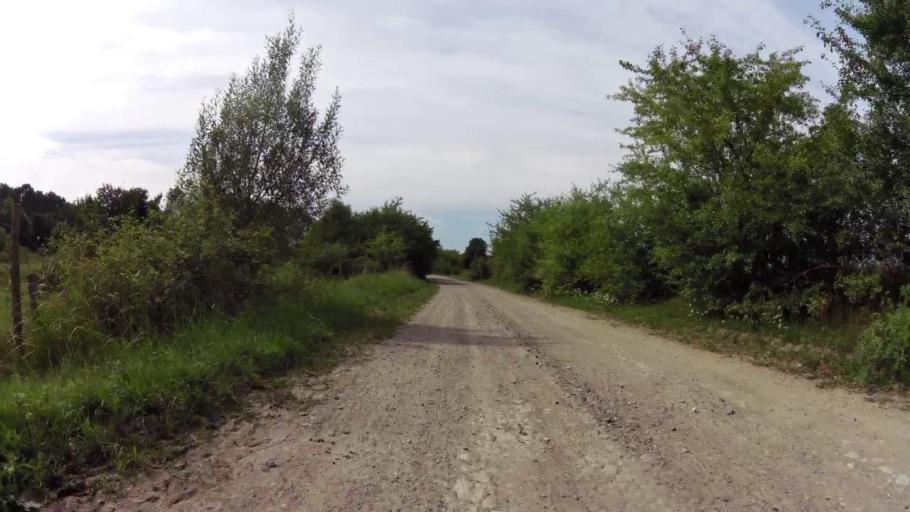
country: PL
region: West Pomeranian Voivodeship
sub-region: Powiat lobeski
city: Wegorzyno
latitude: 53.5379
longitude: 15.6071
